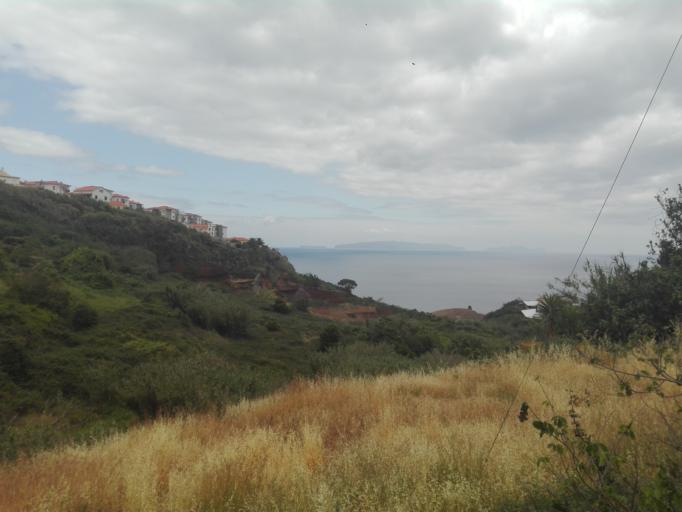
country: PT
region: Madeira
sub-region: Santa Cruz
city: Camacha
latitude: 32.6566
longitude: -16.8265
